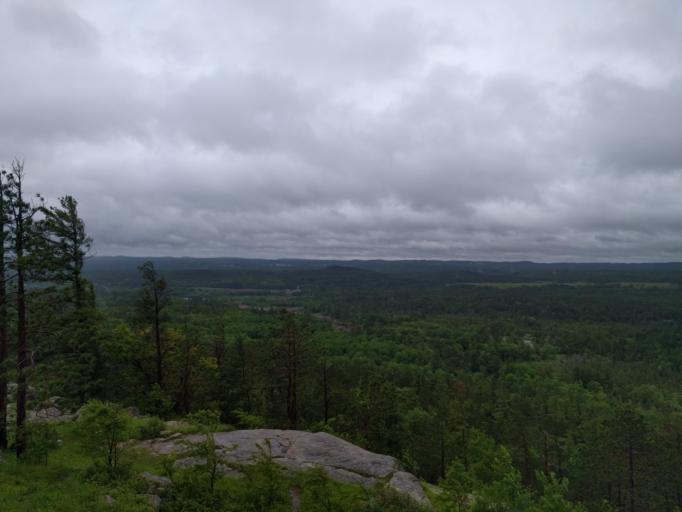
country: US
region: Michigan
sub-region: Marquette County
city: Trowbridge Park
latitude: 46.6045
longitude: -87.4556
